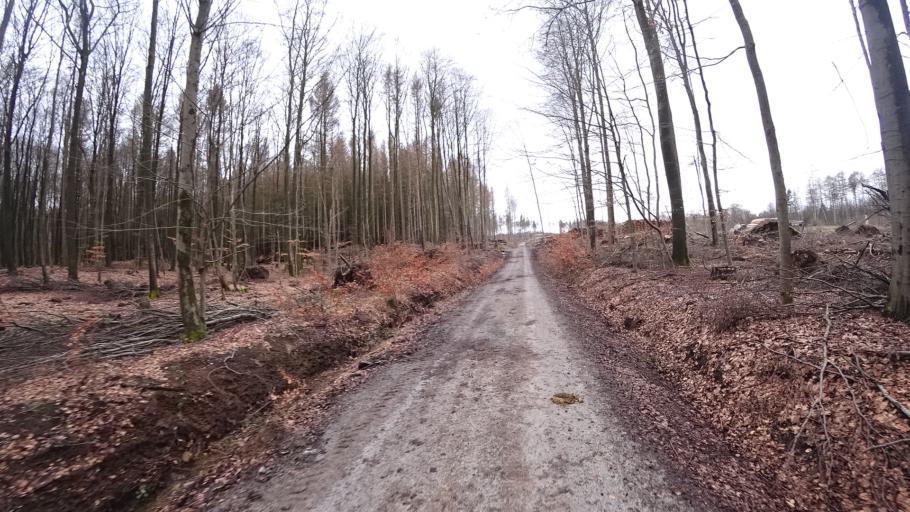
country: DE
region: Rheinland-Pfalz
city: Dernbach
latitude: 50.4351
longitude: 7.7779
